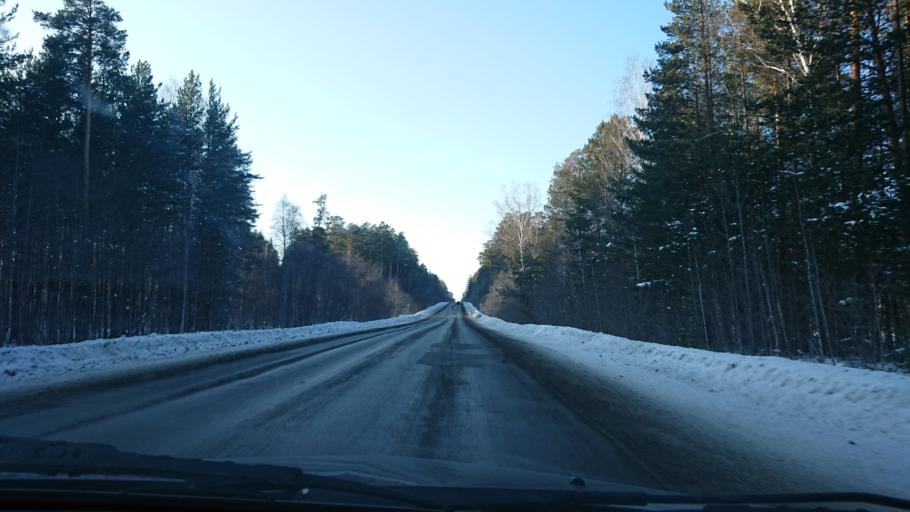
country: RU
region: Sverdlovsk
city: Gornyy Shchit
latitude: 56.6291
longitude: 60.3384
